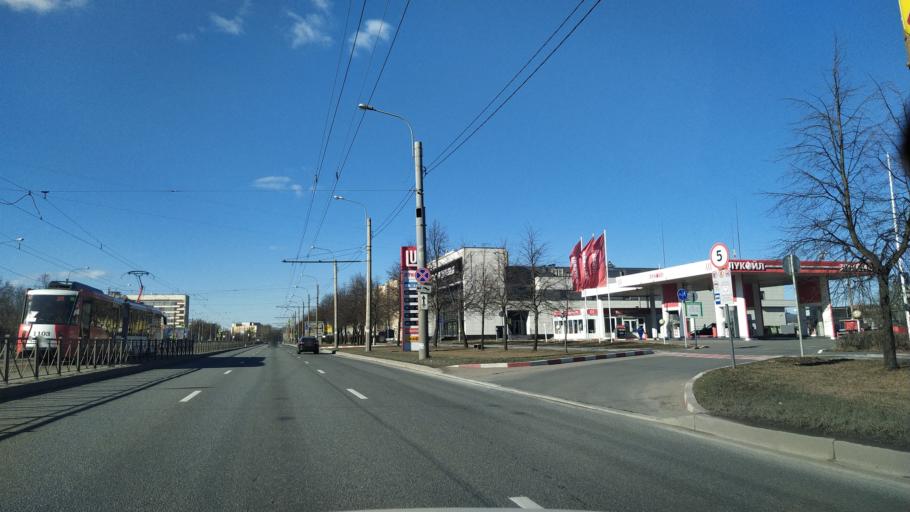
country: RU
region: St.-Petersburg
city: Kupchino
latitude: 59.8890
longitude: 30.3622
